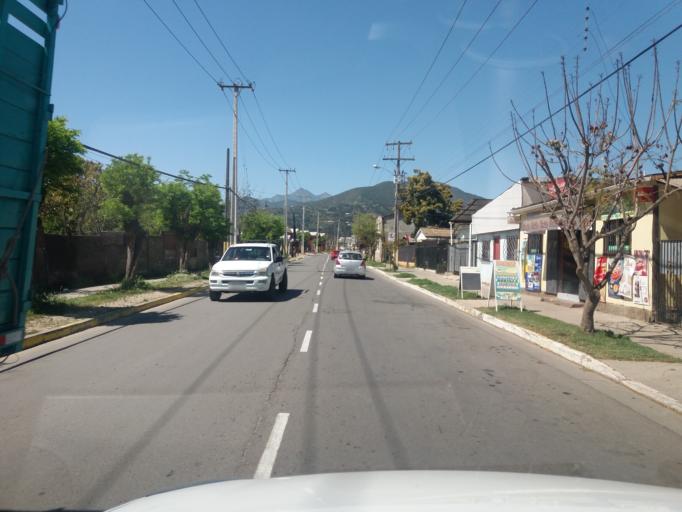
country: CL
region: Valparaiso
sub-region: Provincia de Quillota
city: Quillota
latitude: -32.9394
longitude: -71.2810
